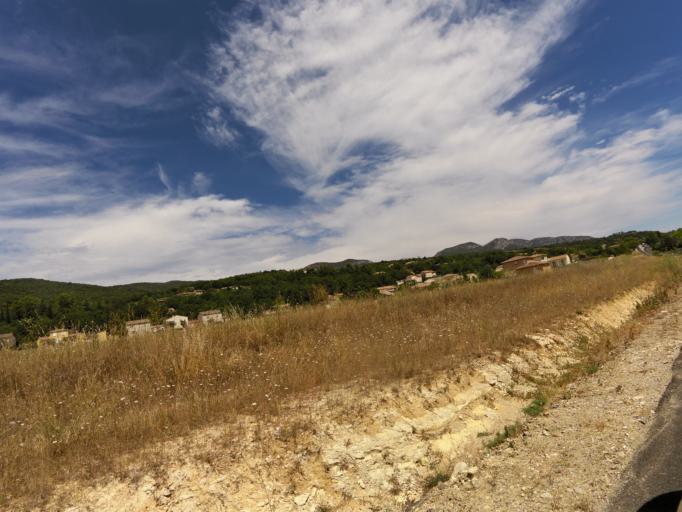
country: FR
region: Languedoc-Roussillon
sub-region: Departement de l'Herault
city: Laroque
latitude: 43.9435
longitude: 3.7273
